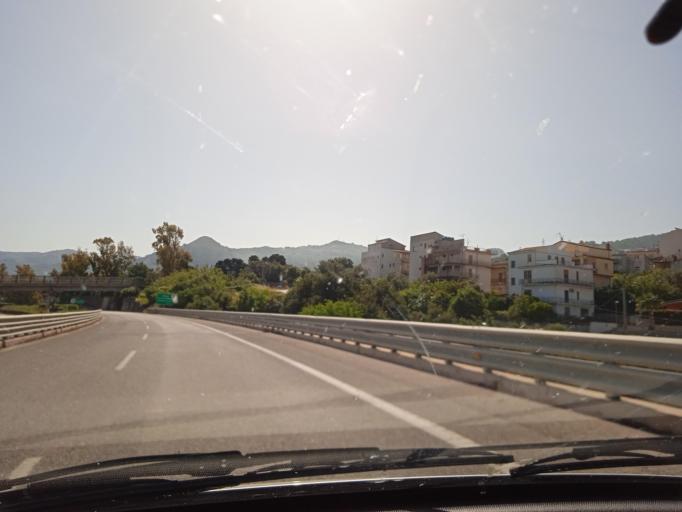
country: IT
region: Sicily
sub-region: Messina
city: Sant'Agata di Militello
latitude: 38.0604
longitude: 14.6326
